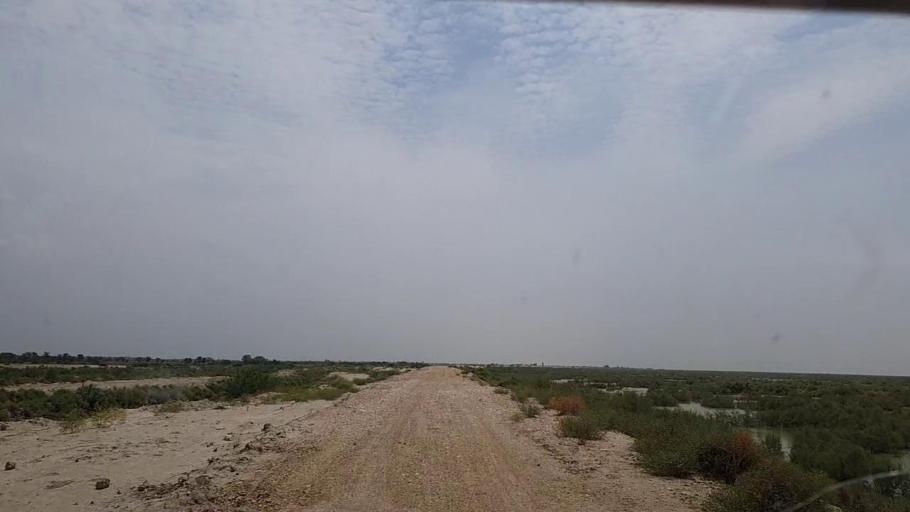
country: PK
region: Sindh
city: Phulji
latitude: 26.8727
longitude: 67.6495
